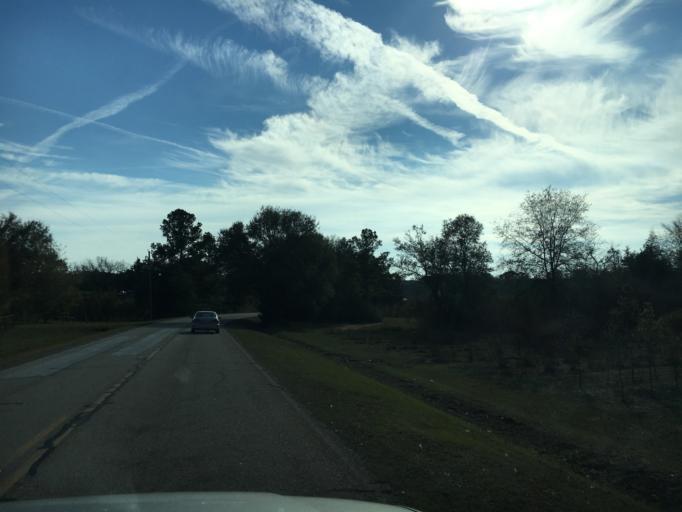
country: US
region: Georgia
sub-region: Hart County
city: Hartwell
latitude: 34.2745
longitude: -82.8704
